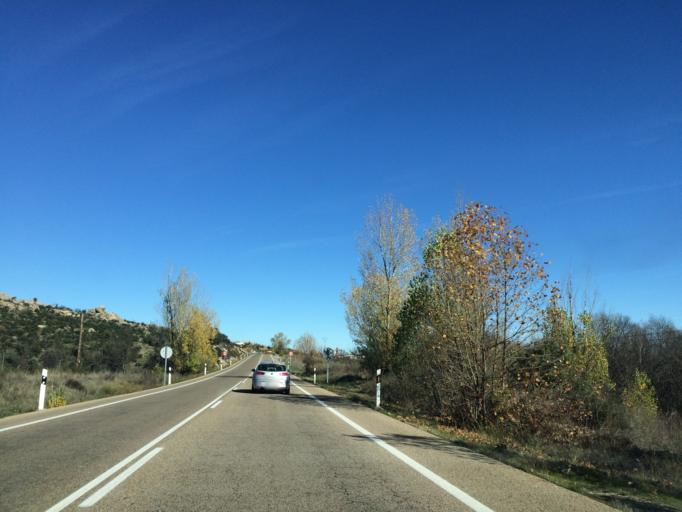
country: ES
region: Madrid
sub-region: Provincia de Madrid
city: Manzanares el Real
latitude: 40.7183
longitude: -3.8854
